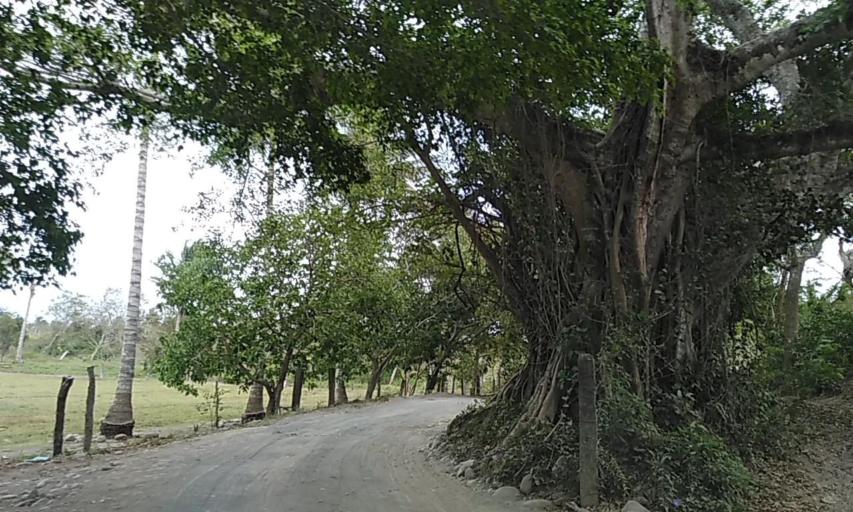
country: MX
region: Veracruz
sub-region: La Antigua
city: Nicolas Blanco (San Pancho)
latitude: 19.3106
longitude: -96.3052
